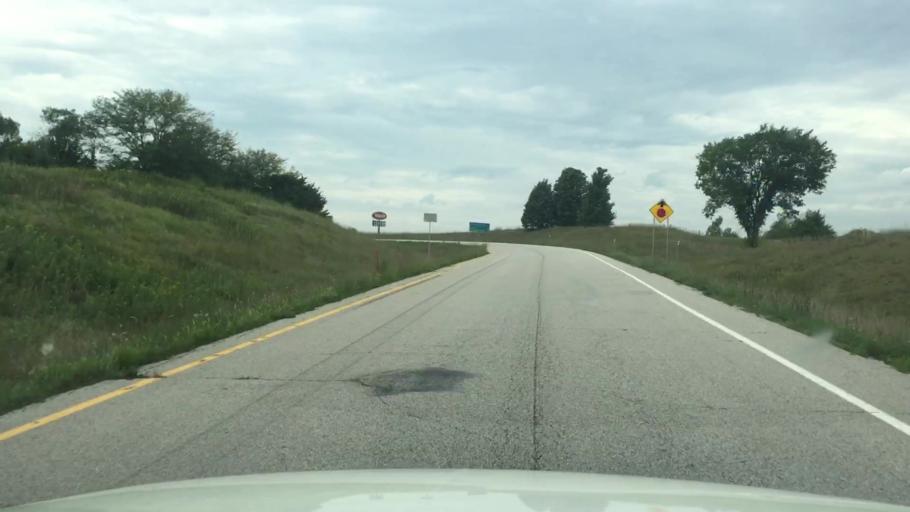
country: US
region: Iowa
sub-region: Decatur County
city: Lamoni
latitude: 40.6254
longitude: -93.8909
